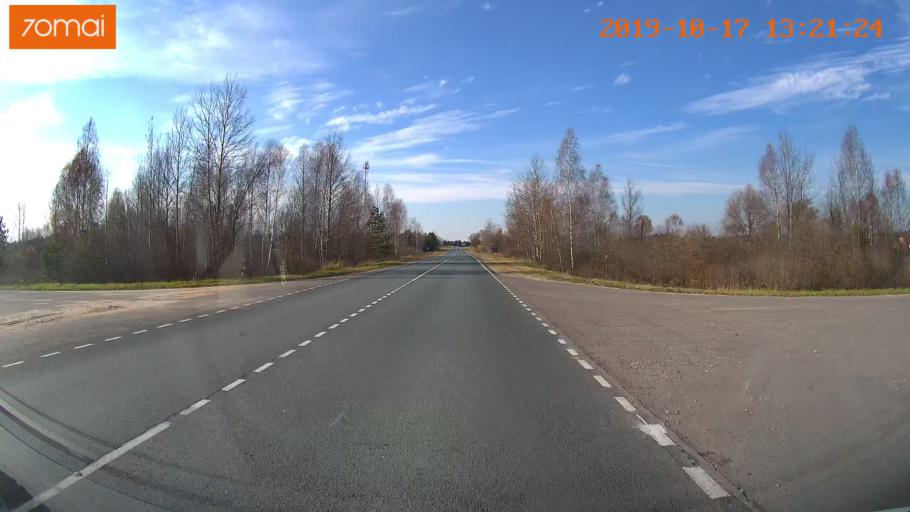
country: RU
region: Rjazan
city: Gus'-Zheleznyy
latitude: 55.0808
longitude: 41.0279
